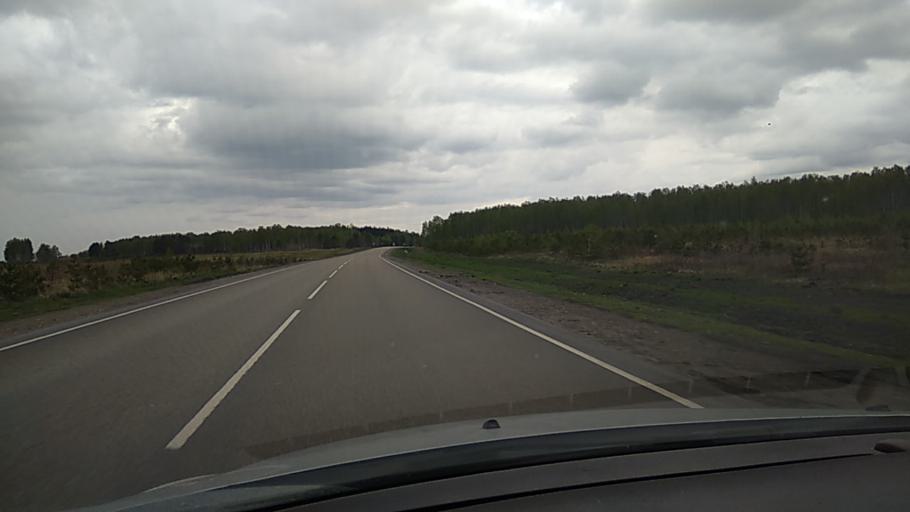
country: RU
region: Kurgan
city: Kataysk
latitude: 56.2965
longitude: 62.4012
